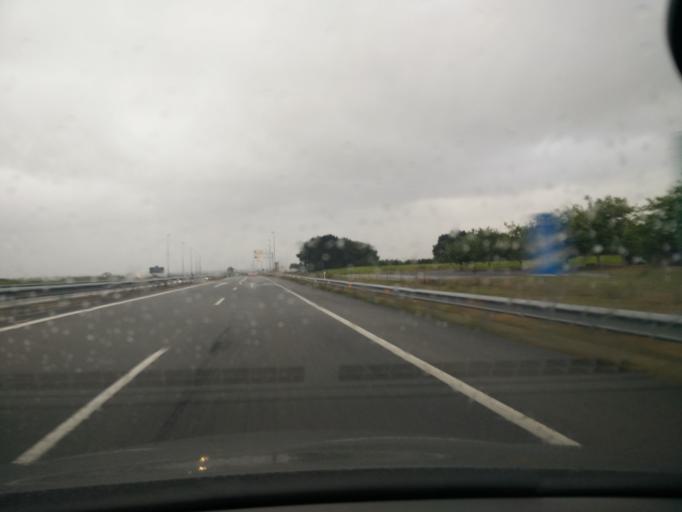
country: ES
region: Asturias
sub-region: Province of Asturias
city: Figueras
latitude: 43.5429
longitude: -7.0292
